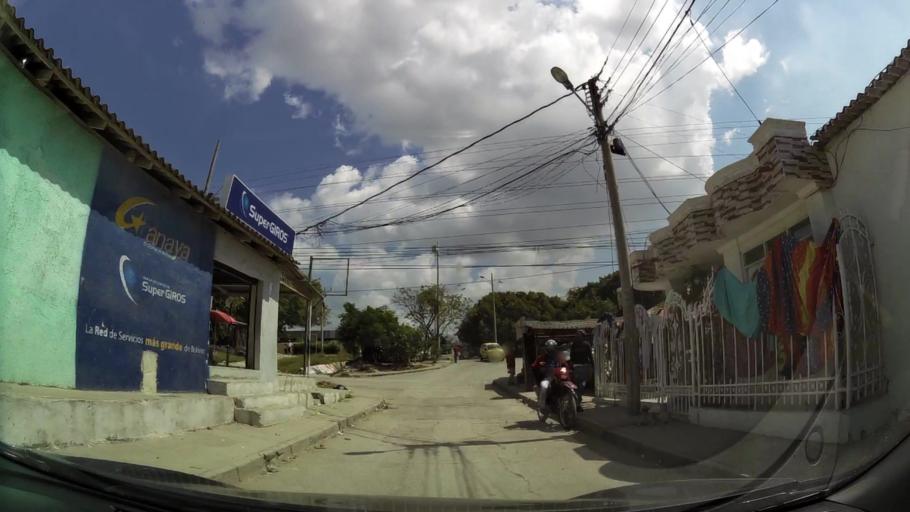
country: CO
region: Bolivar
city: Cartagena
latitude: 10.3687
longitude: -75.5076
